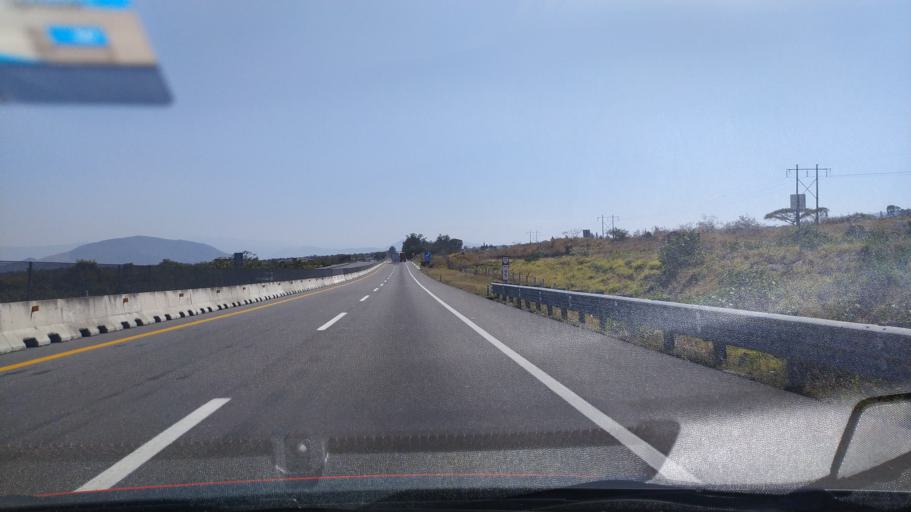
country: MX
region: Jalisco
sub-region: Zapotlan el Grande
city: Ciudad Guzman [CERESO]
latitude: 19.6352
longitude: -103.4674
